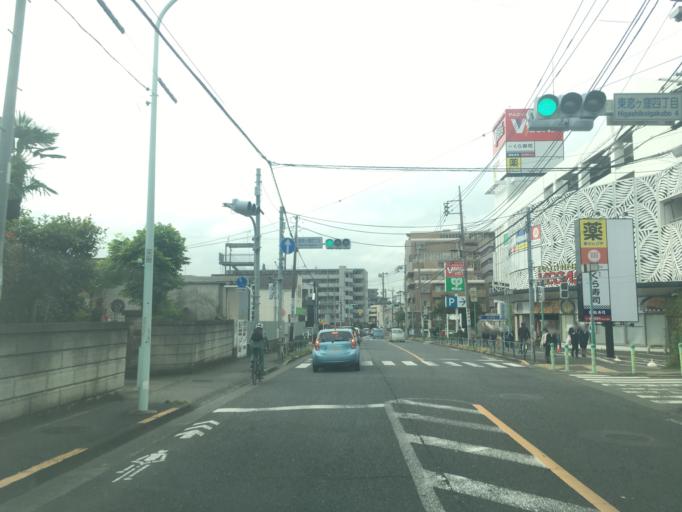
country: JP
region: Tokyo
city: Kokubunji
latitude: 35.7094
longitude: 139.4684
